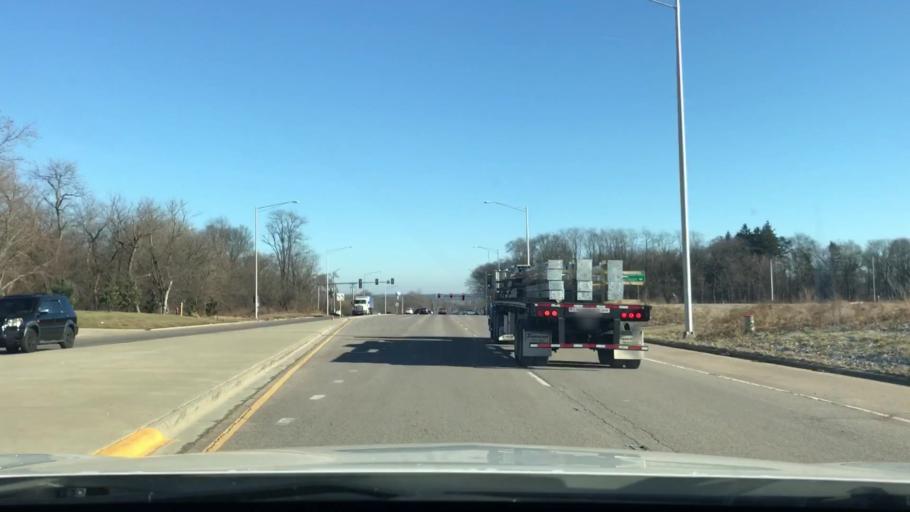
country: US
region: Illinois
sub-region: Kane County
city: Gilberts
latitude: 42.1034
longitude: -88.3378
